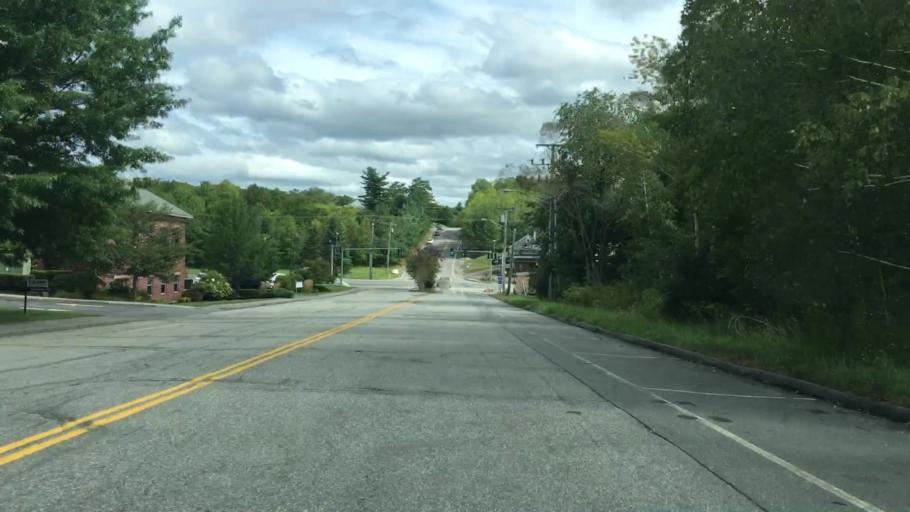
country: US
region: Maine
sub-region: Kennebec County
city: Augusta
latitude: 44.3404
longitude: -69.7947
